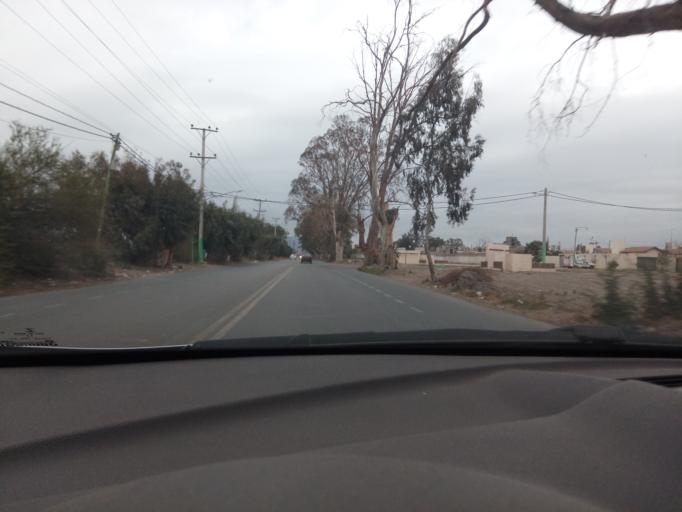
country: AR
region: San Juan
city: San Juan
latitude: -31.5489
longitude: -68.5760
